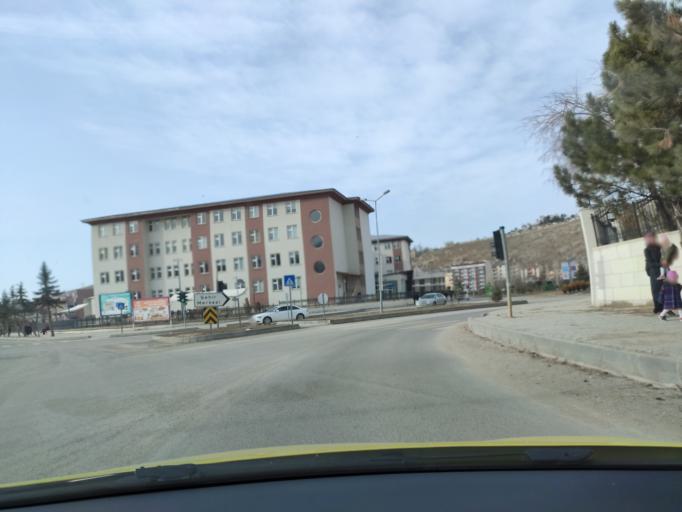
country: TR
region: Bayburt
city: Bayburt
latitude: 40.2490
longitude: 40.2320
